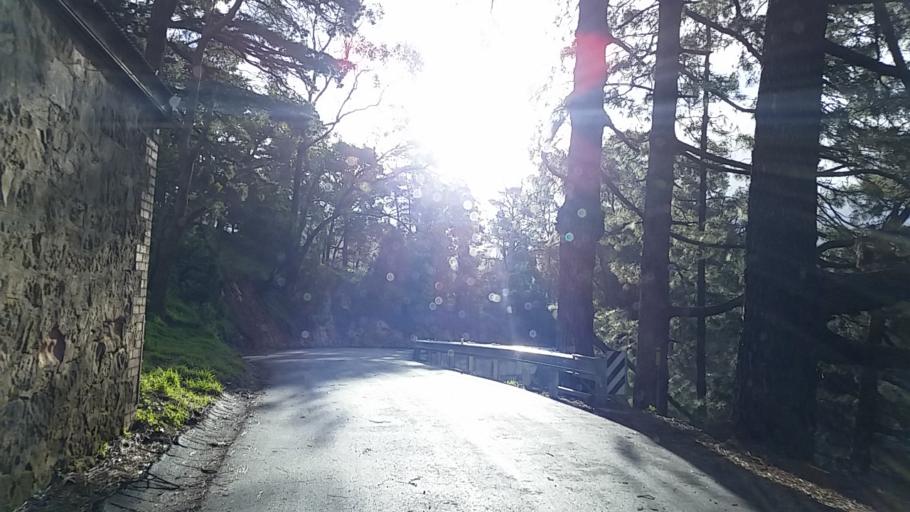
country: AU
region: South Australia
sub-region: Adelaide Hills
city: Adelaide Hills
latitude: -34.9368
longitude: 138.7674
